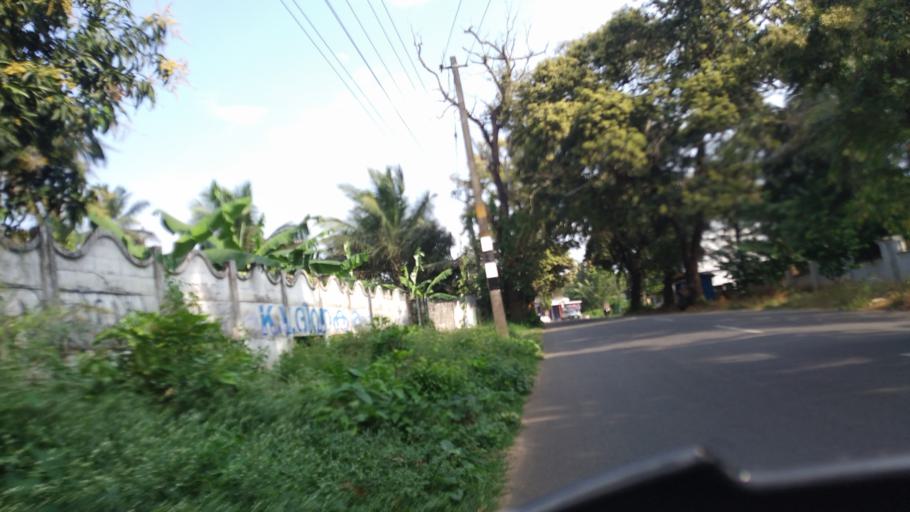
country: IN
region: Kerala
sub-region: Thrissur District
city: Chelakara
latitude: 10.5968
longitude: 76.5007
